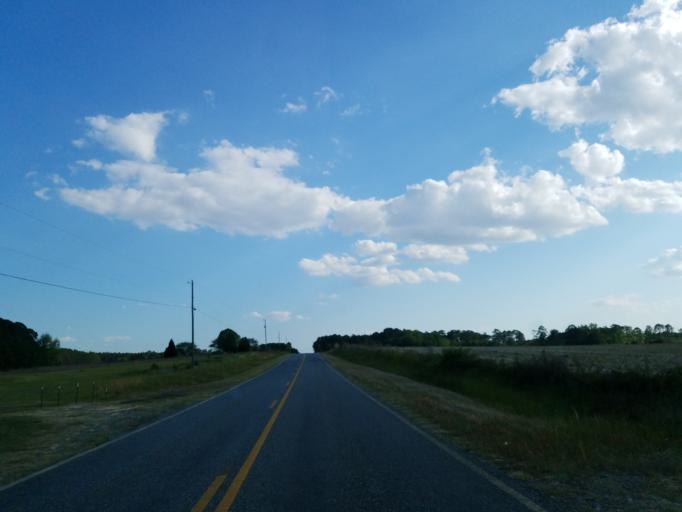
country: US
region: Georgia
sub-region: Tift County
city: Tifton
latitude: 31.5371
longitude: -83.5448
